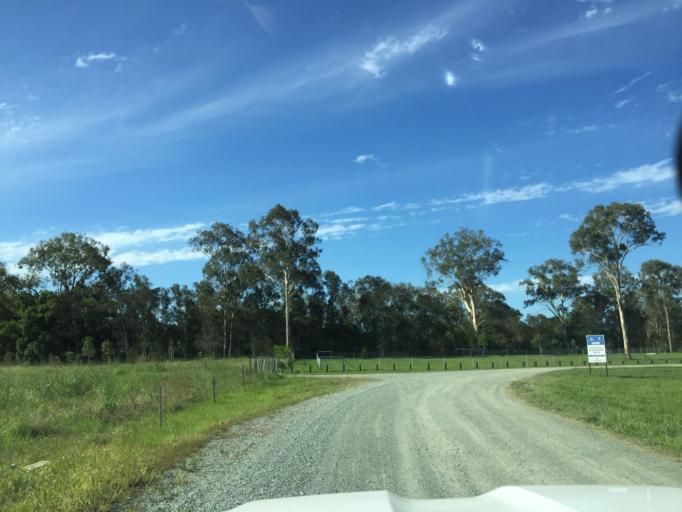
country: AU
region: Queensland
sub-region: Moreton Bay
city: Morayfield
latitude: -27.1072
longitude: 152.9930
